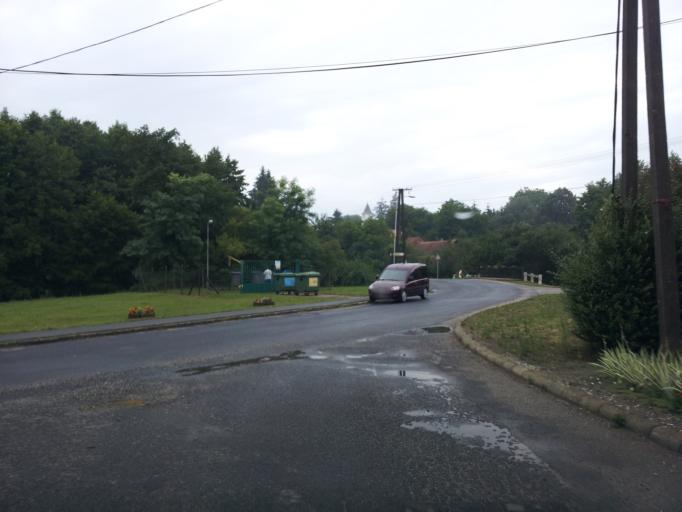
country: HU
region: Zala
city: Zalalovo
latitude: 46.8668
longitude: 16.5484
